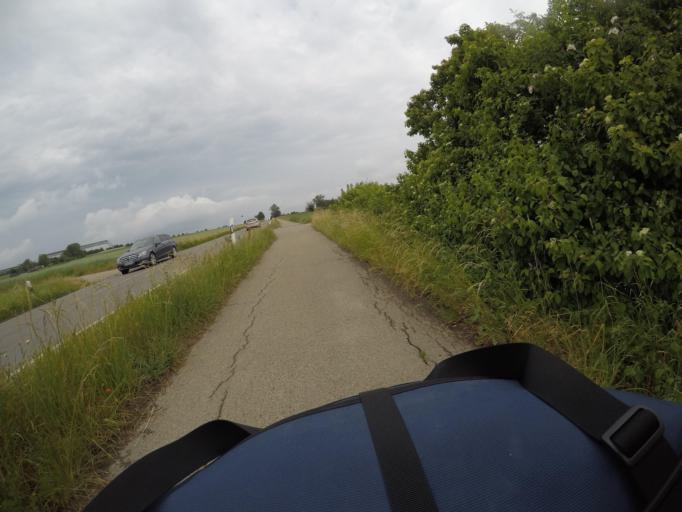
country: DE
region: Baden-Wuerttemberg
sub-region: Regierungsbezirk Stuttgart
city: Gerlingen
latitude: 48.8106
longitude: 9.0695
